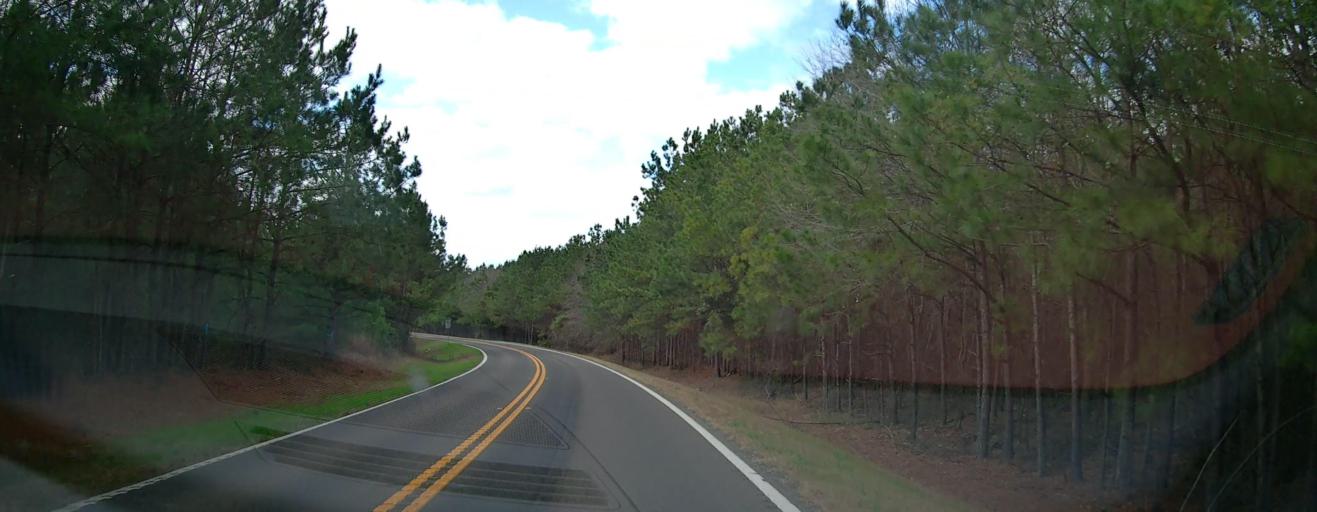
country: US
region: Georgia
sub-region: Marion County
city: Buena Vista
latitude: 32.4331
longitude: -84.4285
